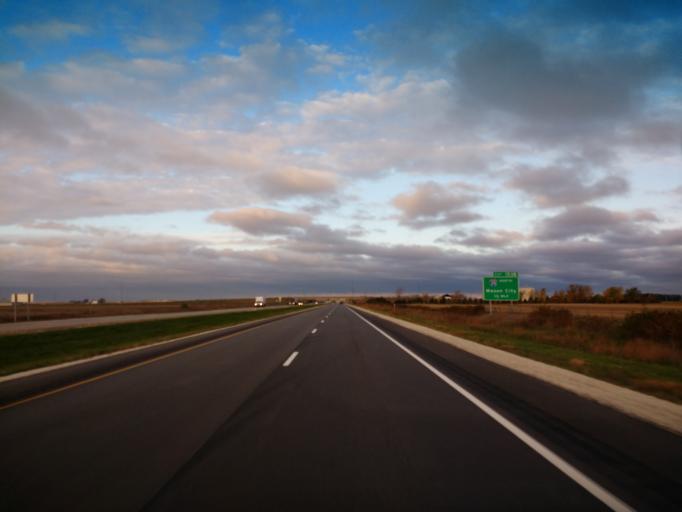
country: US
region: Illinois
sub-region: Knox County
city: Knoxville
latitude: 40.9185
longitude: -90.2936
